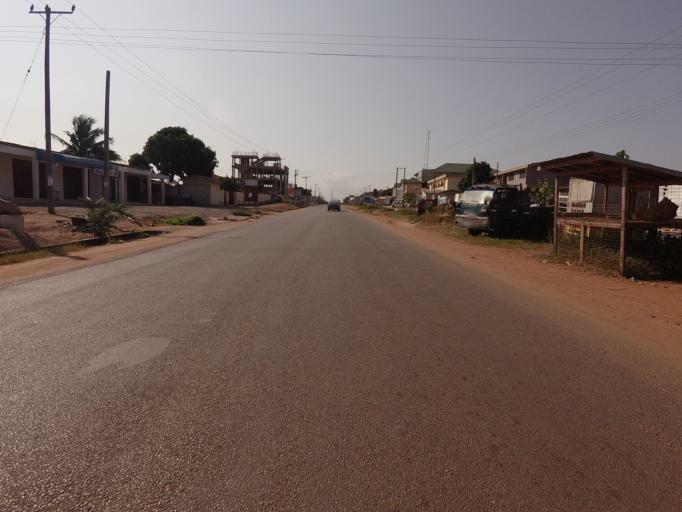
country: GH
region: Greater Accra
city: Teshi Old Town
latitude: 5.6029
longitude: -0.1043
